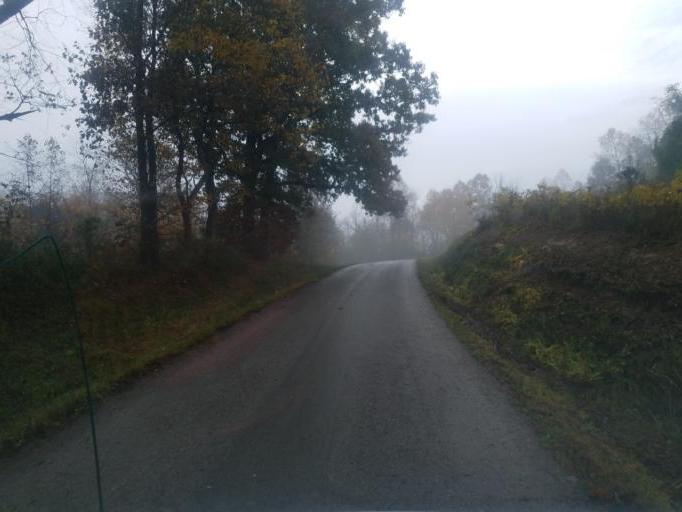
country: US
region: Ohio
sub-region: Morgan County
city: McConnelsville
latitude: 39.4966
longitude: -81.8160
